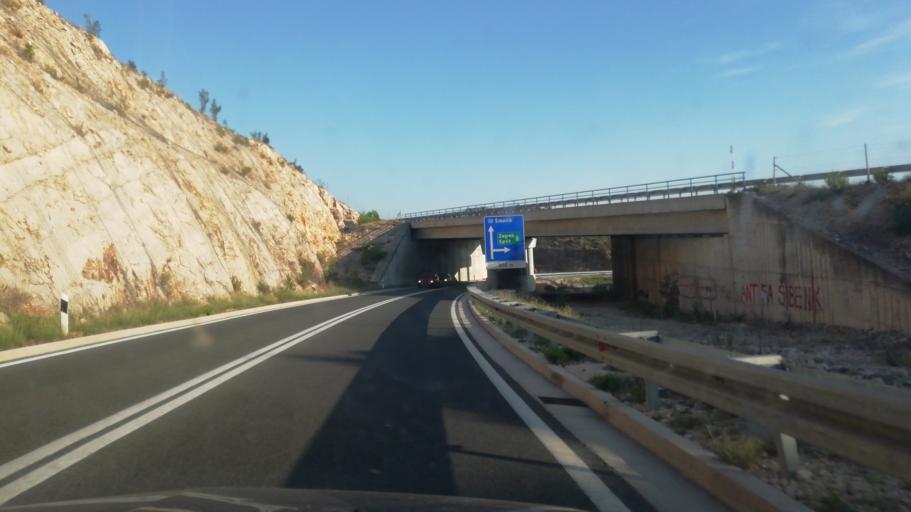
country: HR
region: Sibensko-Kniniska
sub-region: Grad Sibenik
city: Sibenik
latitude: 43.7591
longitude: 15.9395
